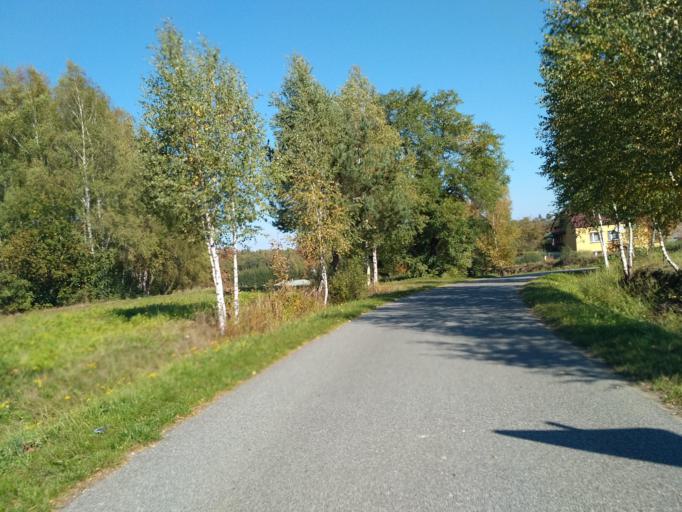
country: PL
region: Subcarpathian Voivodeship
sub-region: Powiat debicki
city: Brzostek
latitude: 49.9470
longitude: 21.3821
